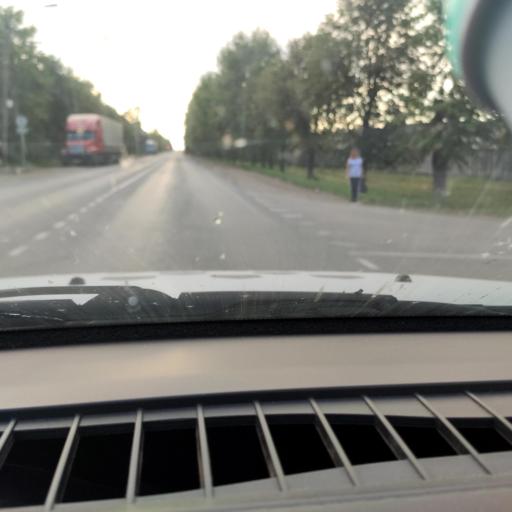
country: RU
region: Kirov
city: Slobodskoy
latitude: 58.7242
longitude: 50.1675
